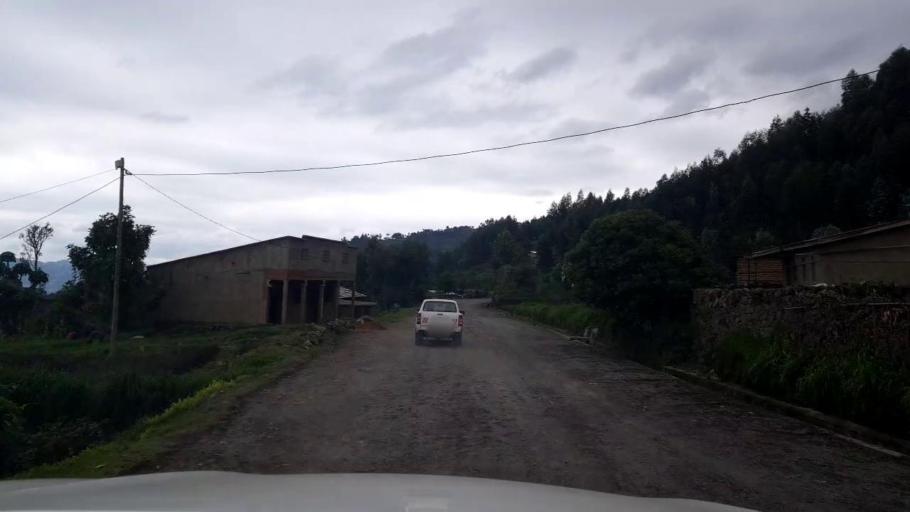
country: RW
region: Northern Province
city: Musanze
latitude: -1.5006
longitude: 29.5340
